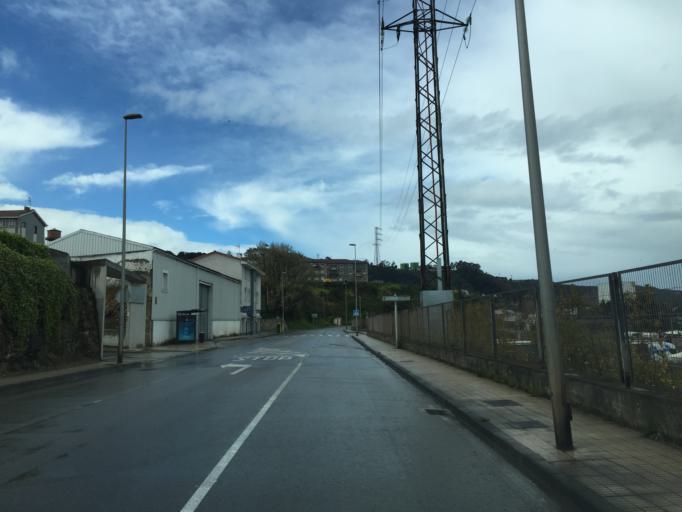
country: ES
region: Asturias
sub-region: Province of Asturias
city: Natahoyo
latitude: 43.5520
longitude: -5.7006
